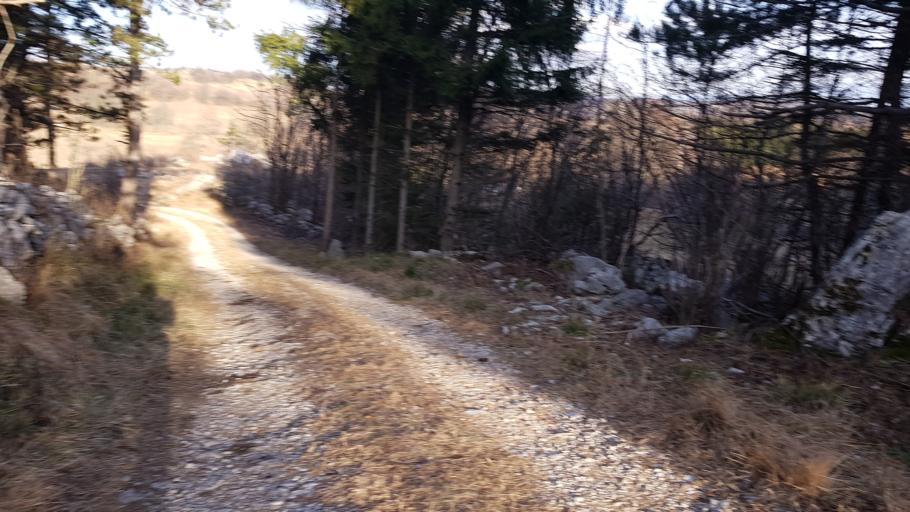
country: SI
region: Nova Gorica
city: Solkan
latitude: 46.0296
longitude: 13.6884
